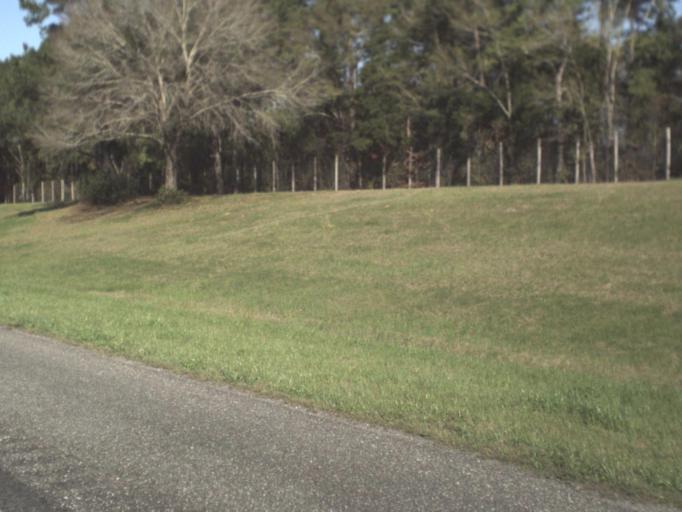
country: US
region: Florida
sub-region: Leon County
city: Tallahassee
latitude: 30.4783
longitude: -84.1176
